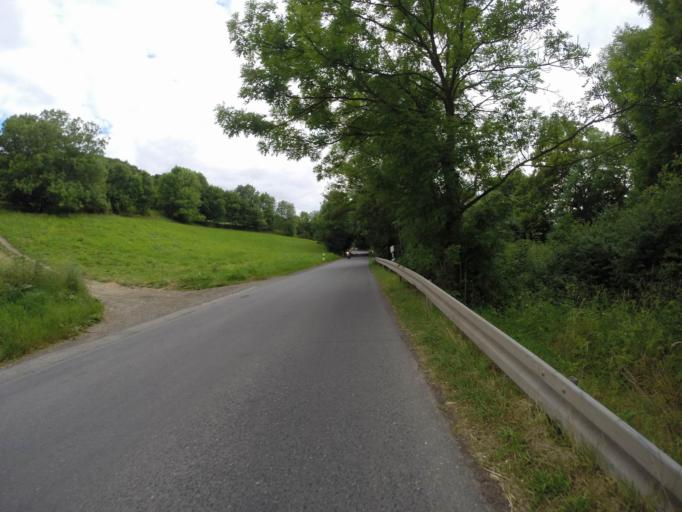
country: DE
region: Thuringia
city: Neuengonna
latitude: 50.9656
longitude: 11.6466
